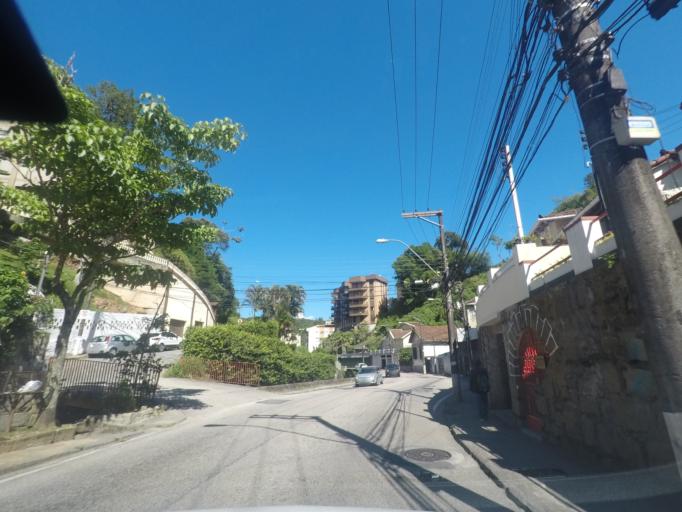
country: BR
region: Rio de Janeiro
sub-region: Petropolis
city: Petropolis
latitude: -22.5219
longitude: -43.1849
